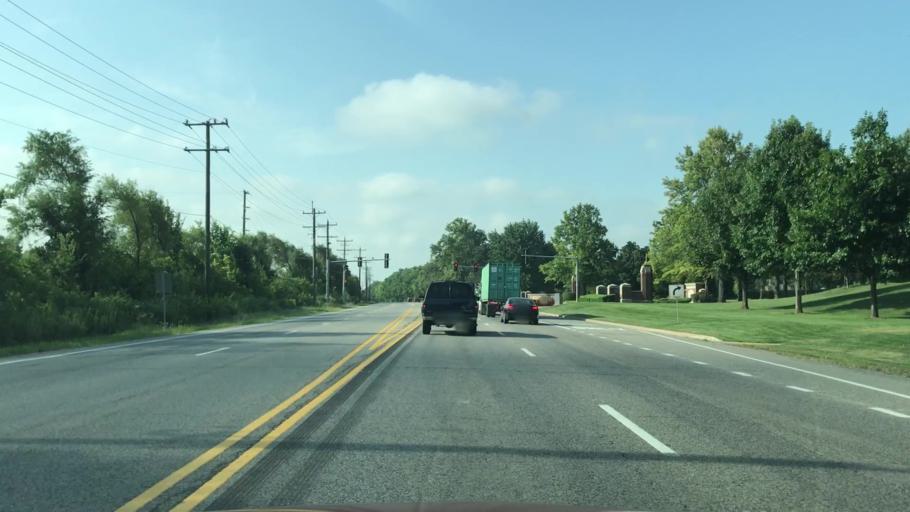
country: US
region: Illinois
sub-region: Will County
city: Lockport
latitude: 41.6067
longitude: -88.0754
